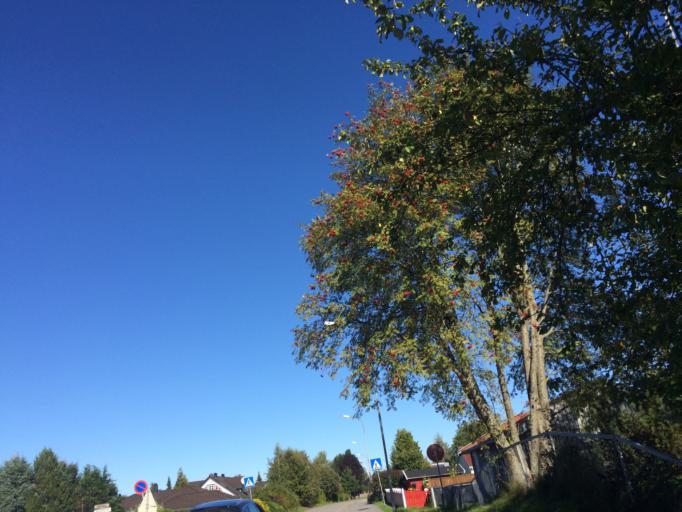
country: NO
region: Akershus
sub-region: Ski
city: Ski
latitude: 59.7160
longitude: 10.8147
